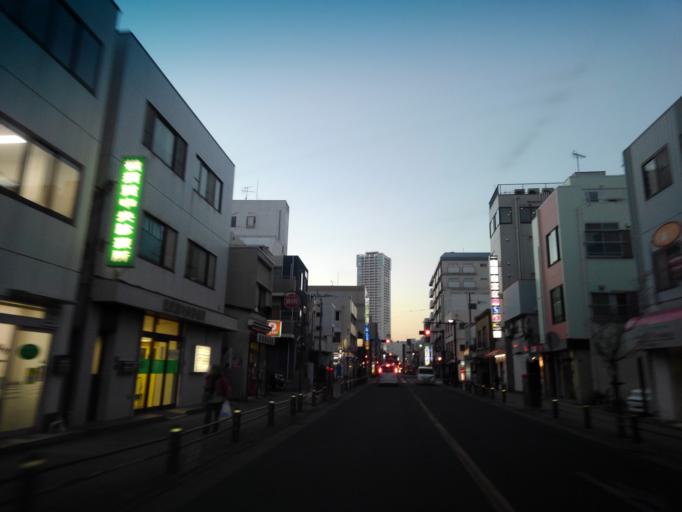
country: JP
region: Kanagawa
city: Yokosuka
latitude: 35.2772
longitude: 139.6755
